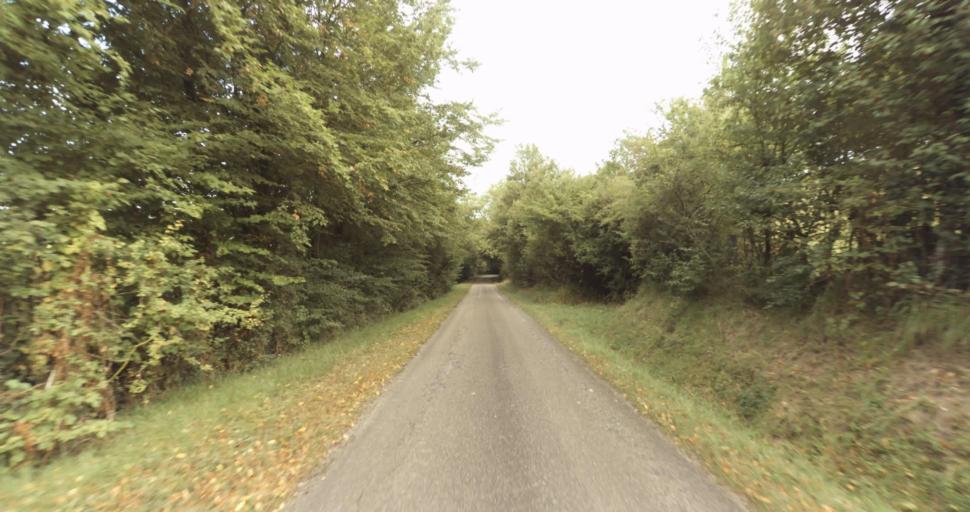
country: FR
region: Lower Normandy
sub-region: Departement de l'Orne
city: Vimoutiers
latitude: 48.8954
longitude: 0.2223
